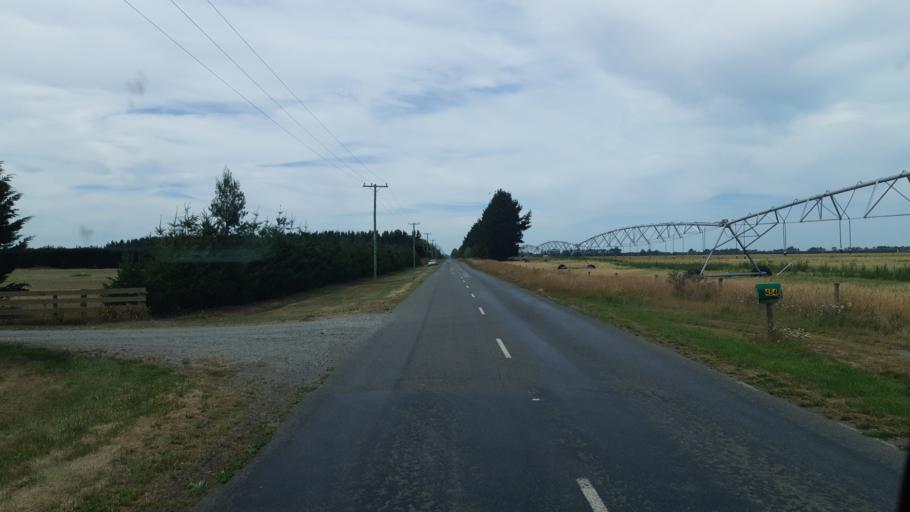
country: NZ
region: Canterbury
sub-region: Ashburton District
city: Tinwald
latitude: -43.9322
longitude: 171.6549
